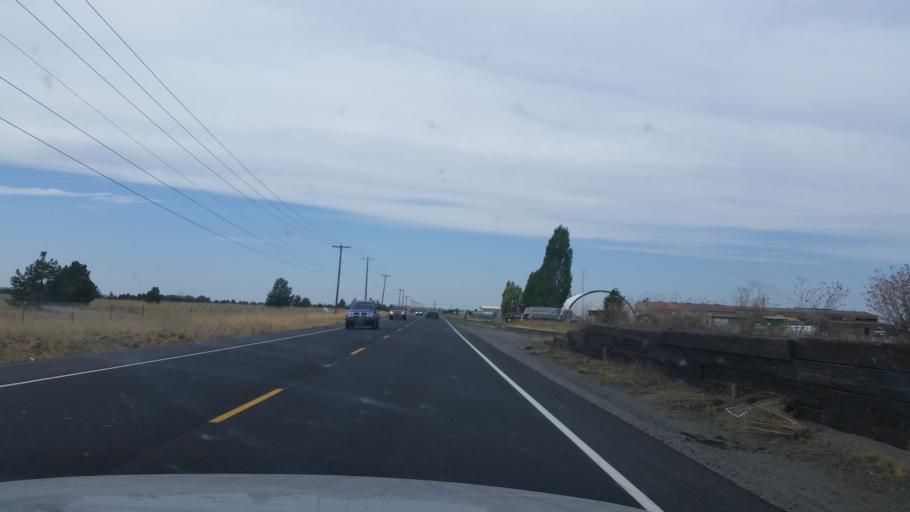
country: US
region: Washington
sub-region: Spokane County
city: Airway Heights
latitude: 47.6284
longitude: -117.5701
